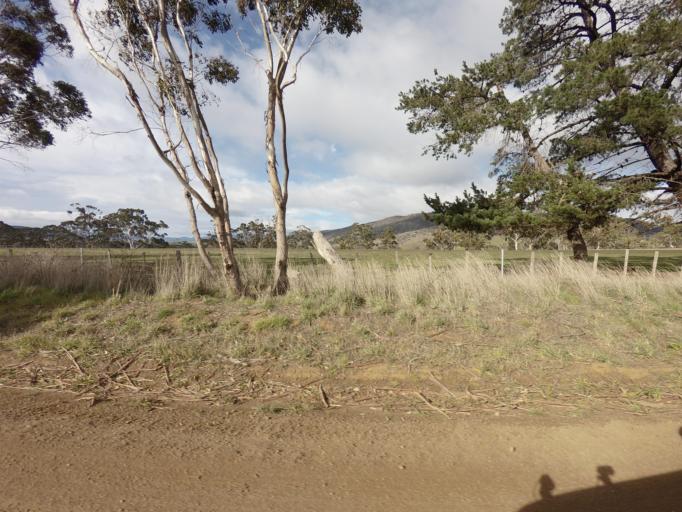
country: AU
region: Tasmania
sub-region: Derwent Valley
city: New Norfolk
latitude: -42.7148
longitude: 146.8849
